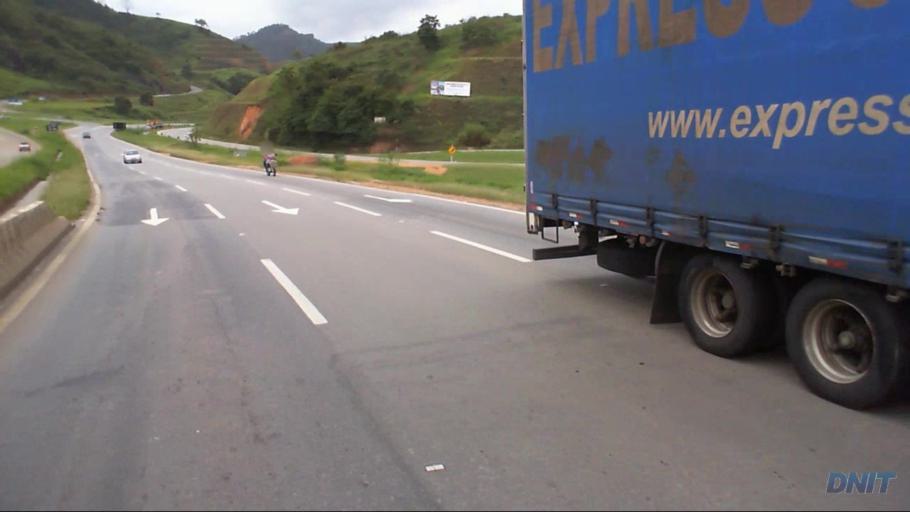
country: BR
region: Minas Gerais
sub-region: Nova Era
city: Nova Era
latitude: -19.7561
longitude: -43.0273
